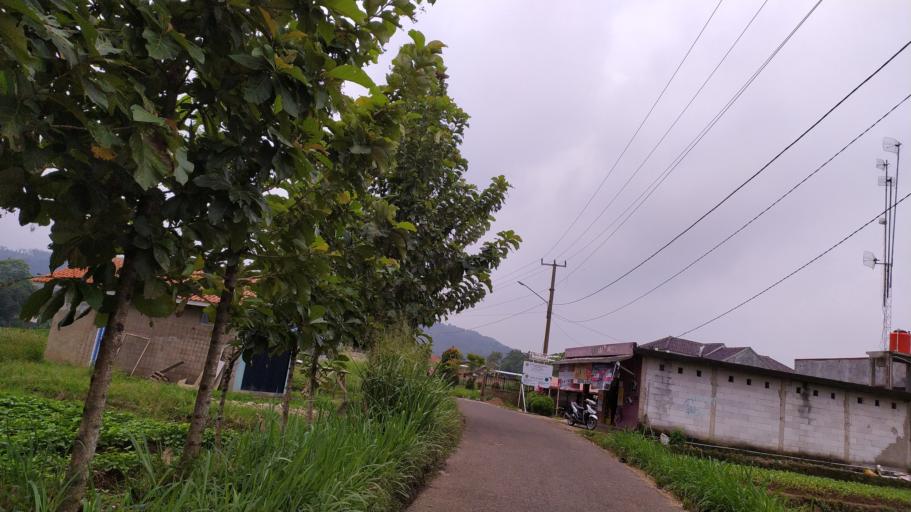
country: ID
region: West Java
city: Ciampea
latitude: -6.6132
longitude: 106.7094
